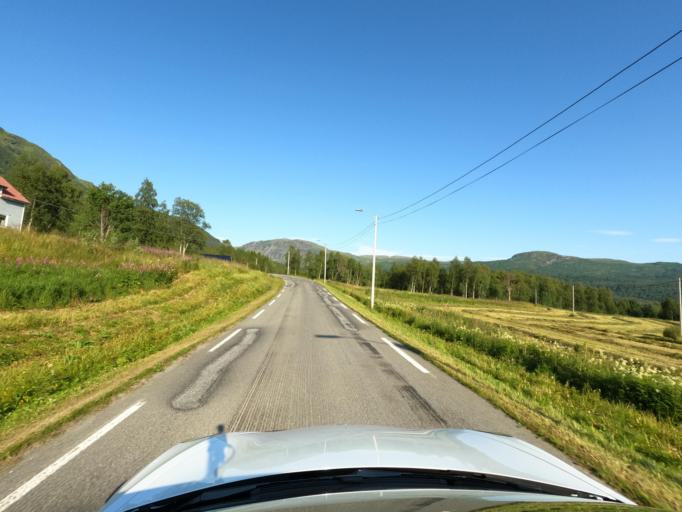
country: NO
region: Troms
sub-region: Gratangen
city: Gratangen
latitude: 68.5611
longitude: 17.6970
